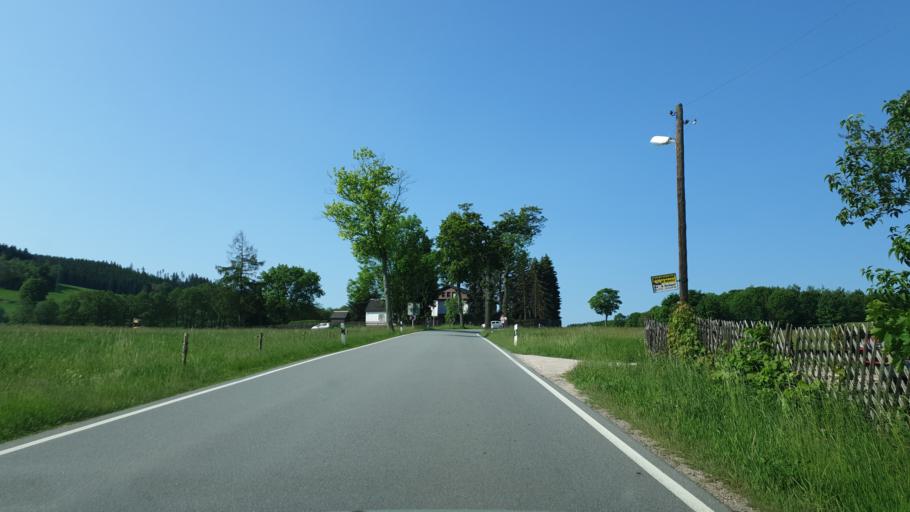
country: DE
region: Saxony
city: Zschorlau
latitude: 50.5593
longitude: 12.6321
